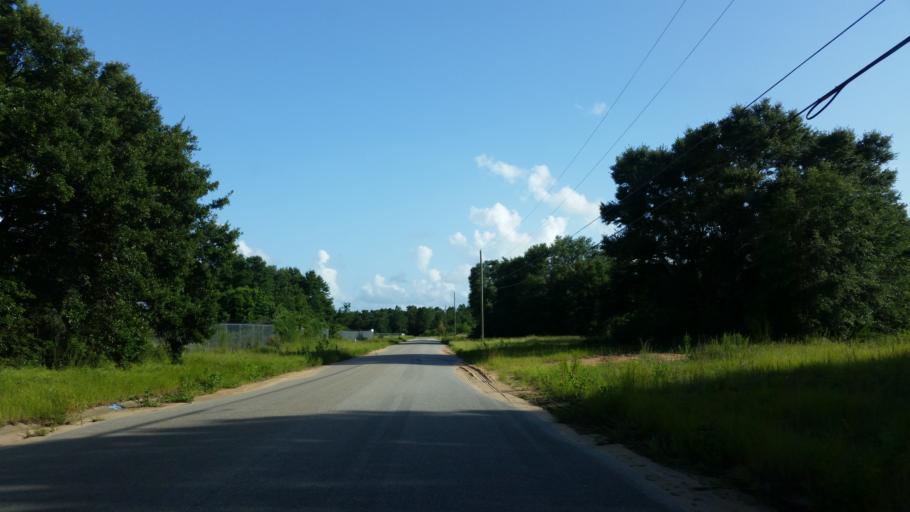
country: US
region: Florida
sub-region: Santa Rosa County
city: Bagdad
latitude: 30.5852
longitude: -87.0769
